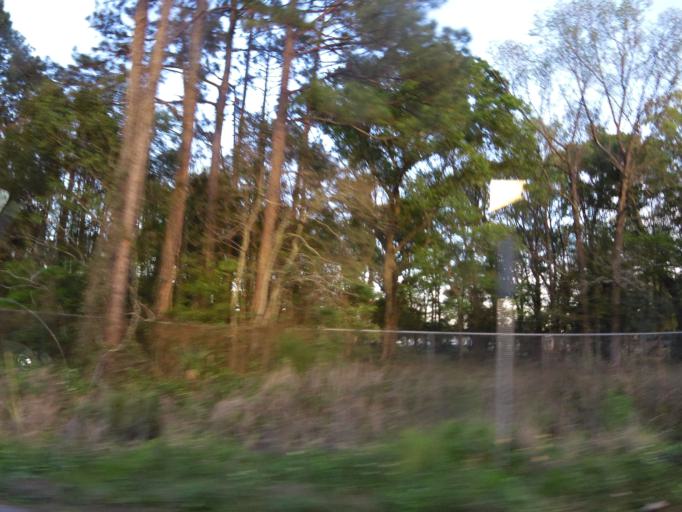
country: US
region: Florida
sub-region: Duval County
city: Jacksonville
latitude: 30.3445
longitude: -81.7292
